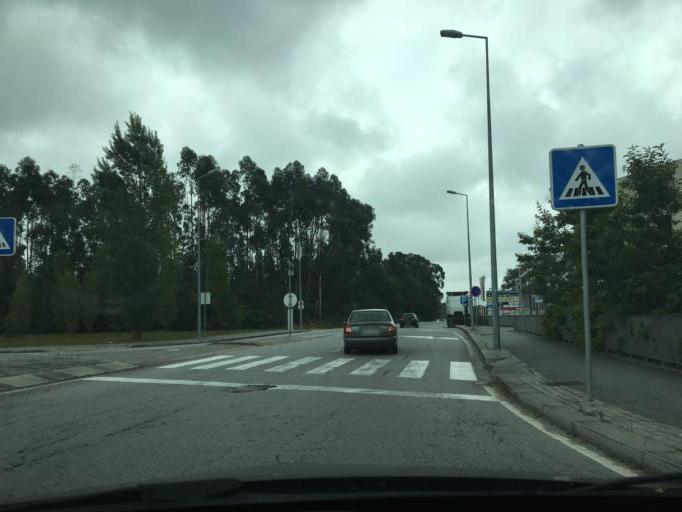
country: PT
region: Porto
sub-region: Maia
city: Maia
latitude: 41.2344
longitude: -8.6396
